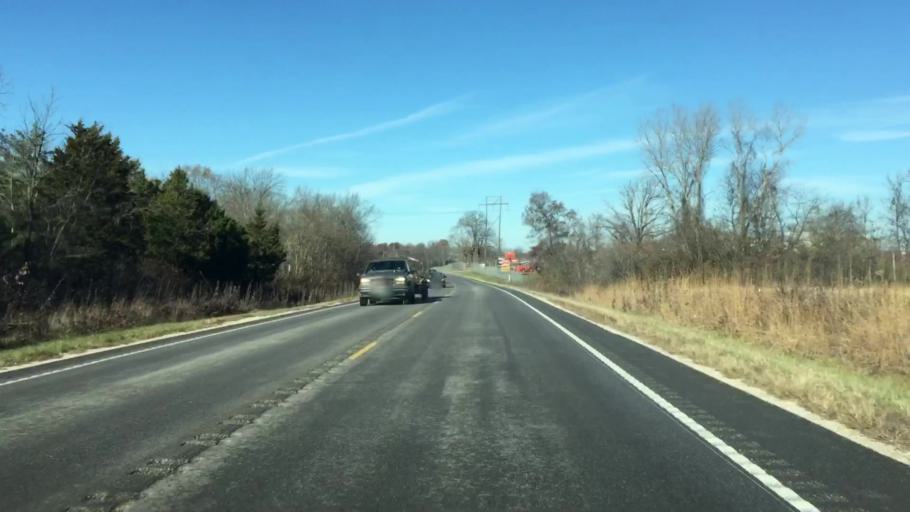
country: US
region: Missouri
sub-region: Miller County
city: Eldon
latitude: 38.3602
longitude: -92.6050
